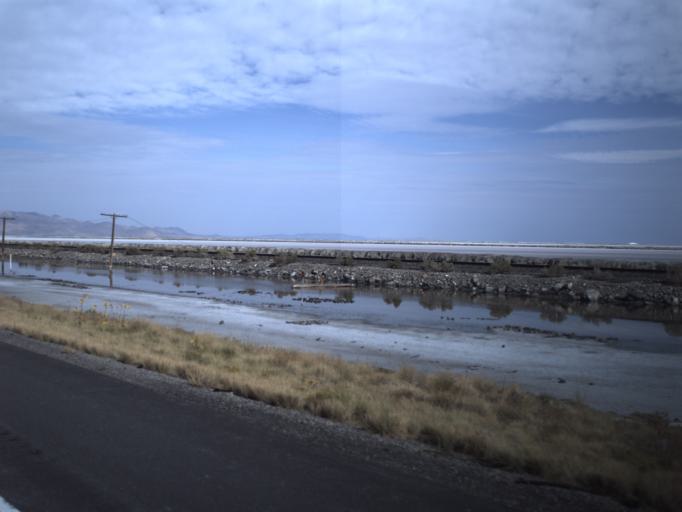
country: US
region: Utah
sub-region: Tooele County
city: Grantsville
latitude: 40.7215
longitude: -112.5578
